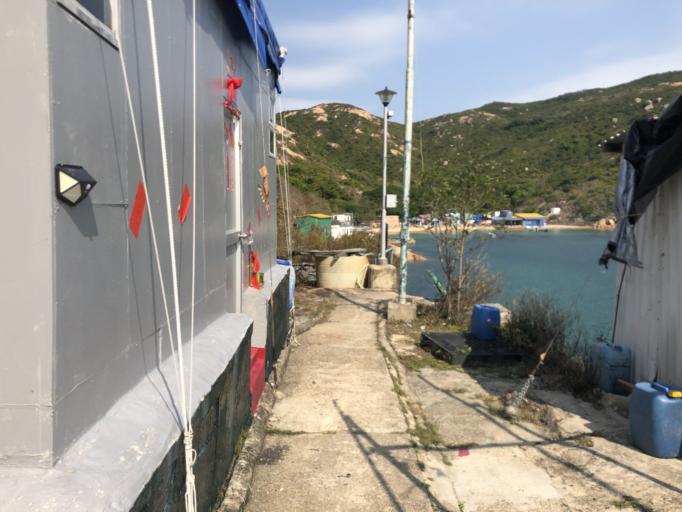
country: HK
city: Sok Kwu Wan
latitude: 22.1646
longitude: 114.2517
